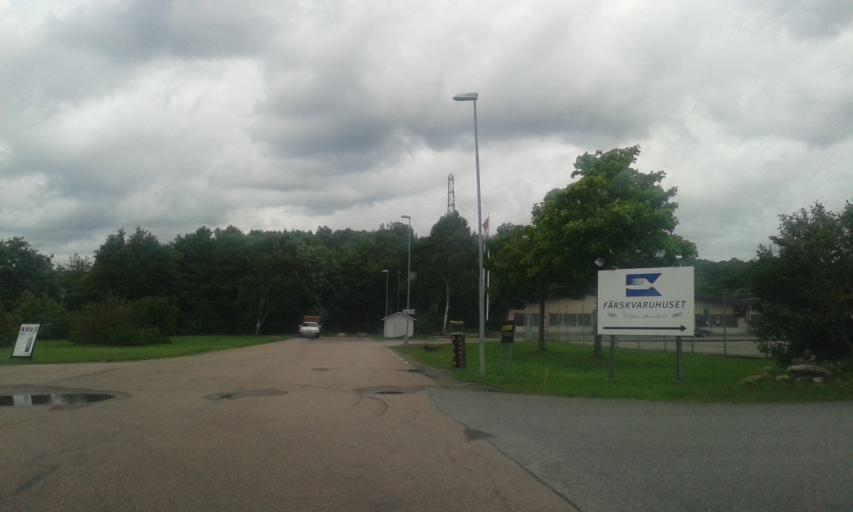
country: SE
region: Vaestra Goetaland
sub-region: Kungalvs Kommun
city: Kungalv
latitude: 57.8792
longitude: 11.9497
